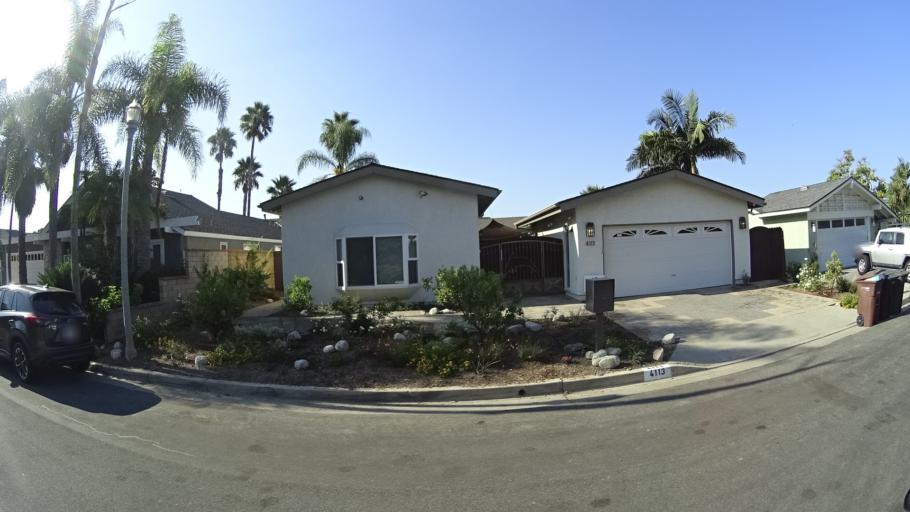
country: US
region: California
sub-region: Orange County
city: San Juan Capistrano
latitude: 33.4662
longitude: -117.6626
